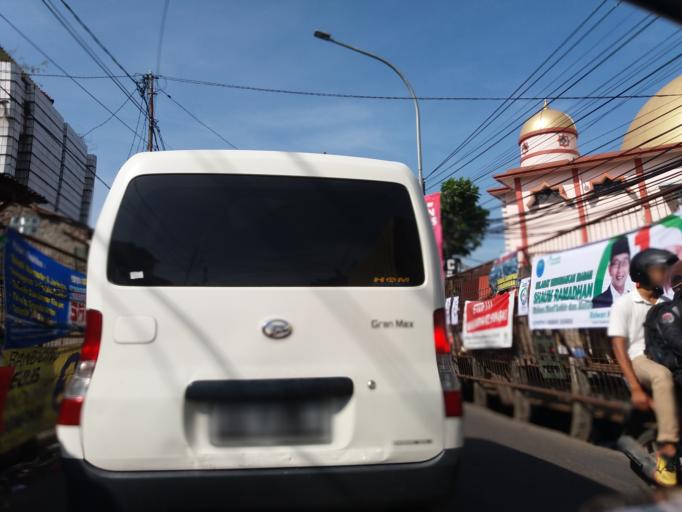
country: ID
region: West Java
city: Bandung
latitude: -6.9543
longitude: 107.6395
